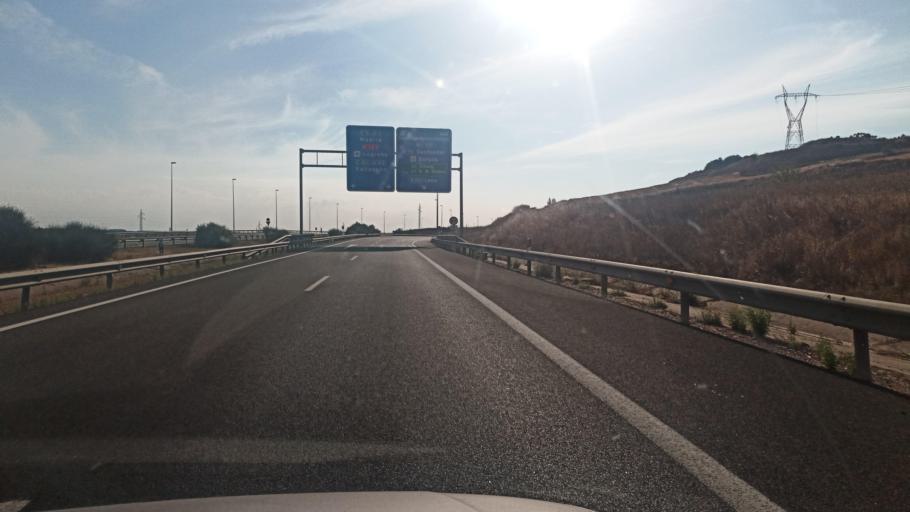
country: ES
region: Castille and Leon
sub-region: Provincia de Burgos
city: Hurones
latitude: 42.3724
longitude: -3.6220
